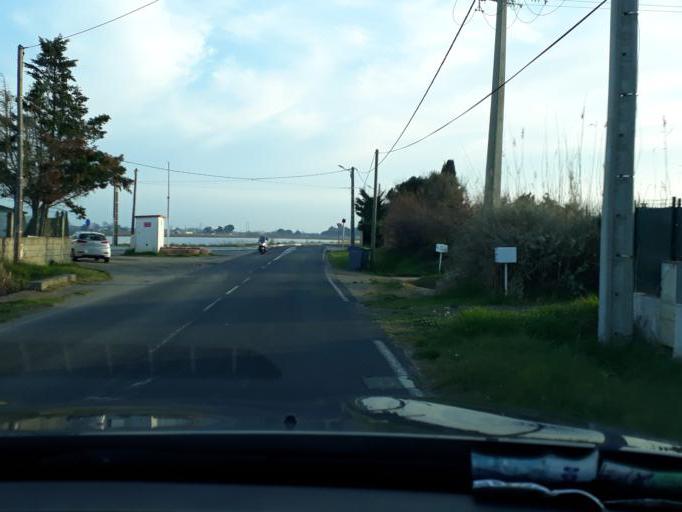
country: FR
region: Languedoc-Roussillon
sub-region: Departement de l'Herault
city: Marseillan
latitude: 43.3299
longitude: 3.5321
